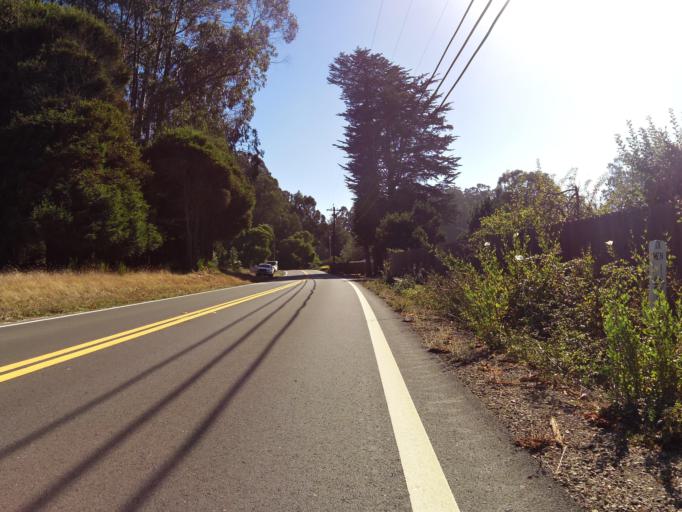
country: US
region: California
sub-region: Mendocino County
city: Fort Bragg
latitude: 39.5247
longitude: -123.7608
